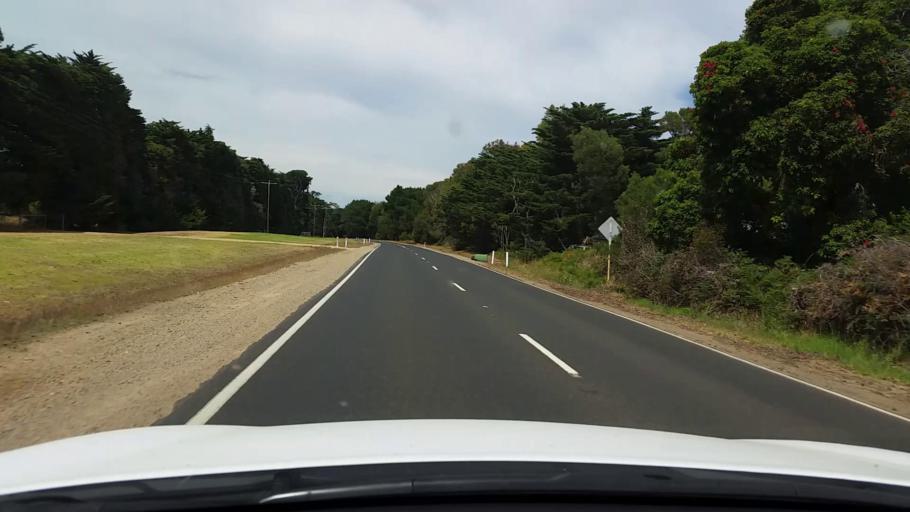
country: AU
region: Victoria
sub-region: Mornington Peninsula
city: Merricks
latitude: -38.4543
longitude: 145.0201
